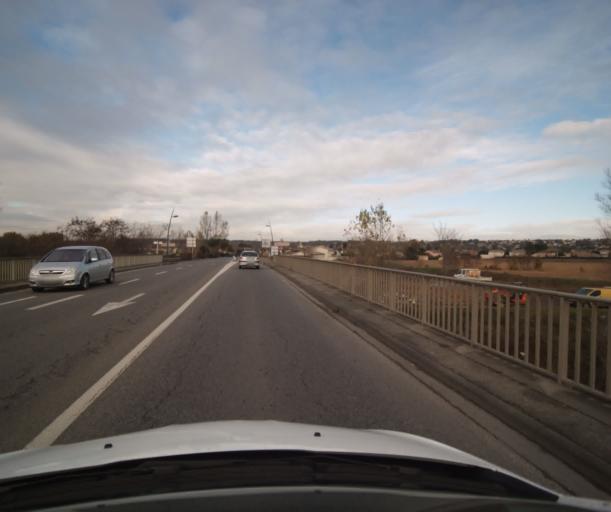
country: FR
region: Midi-Pyrenees
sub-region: Departement de la Haute-Garonne
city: Bruguieres
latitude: 43.7176
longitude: 1.4063
